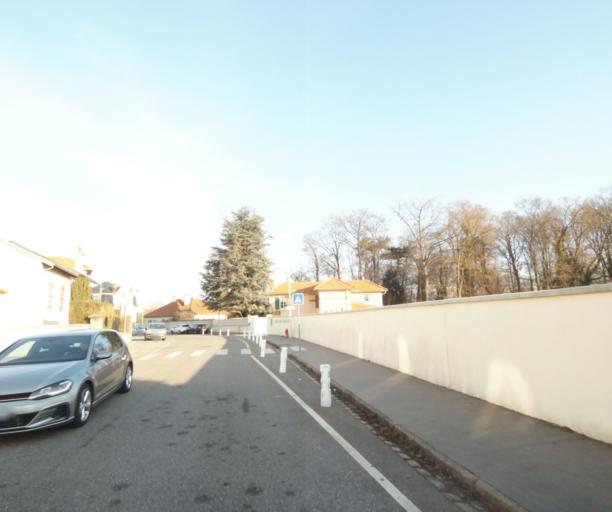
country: FR
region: Lorraine
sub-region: Departement de Meurthe-et-Moselle
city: Laxou
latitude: 48.6944
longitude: 6.1521
